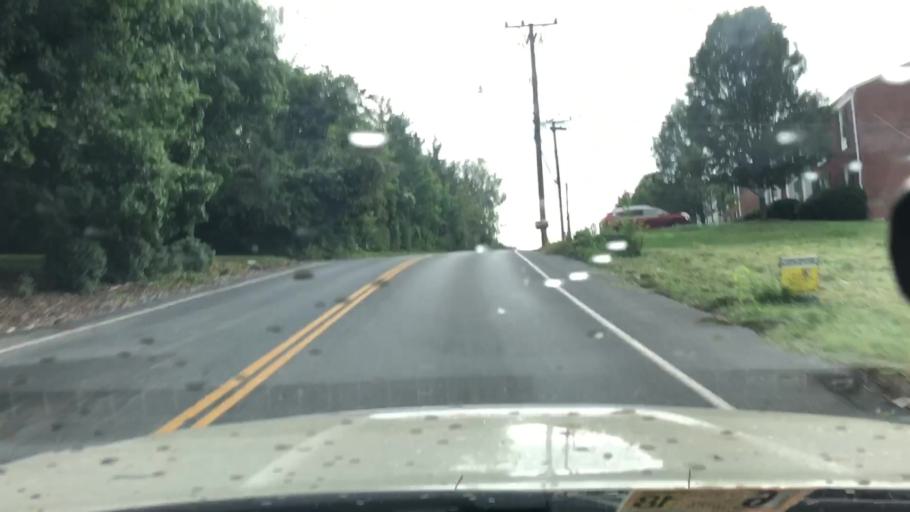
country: US
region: Virginia
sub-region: City of Harrisonburg
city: Harrisonburg
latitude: 38.4296
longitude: -78.8963
